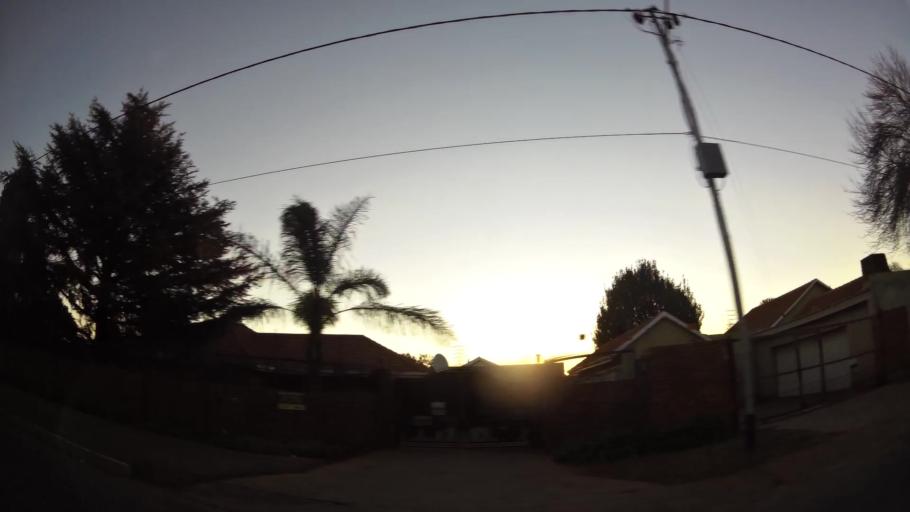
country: ZA
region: Gauteng
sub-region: City of Johannesburg Metropolitan Municipality
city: Roodepoort
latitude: -26.1710
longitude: 27.9157
